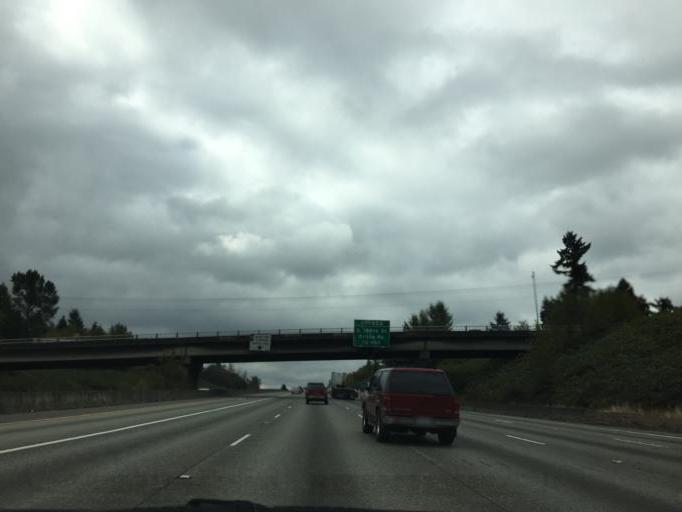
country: US
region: Washington
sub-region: King County
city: SeaTac
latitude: 47.4446
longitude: -122.2680
